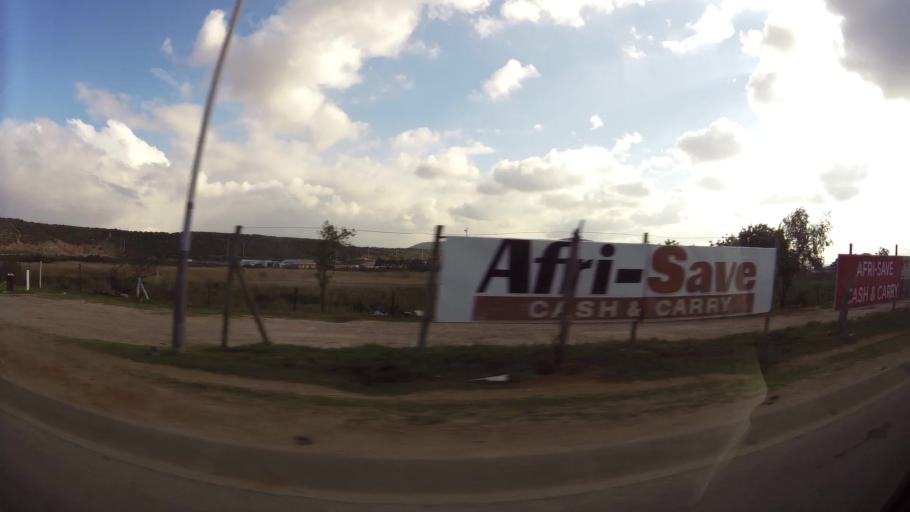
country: ZA
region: Eastern Cape
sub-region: Nelson Mandela Bay Metropolitan Municipality
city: Uitenhage
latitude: -33.7763
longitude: 25.3913
